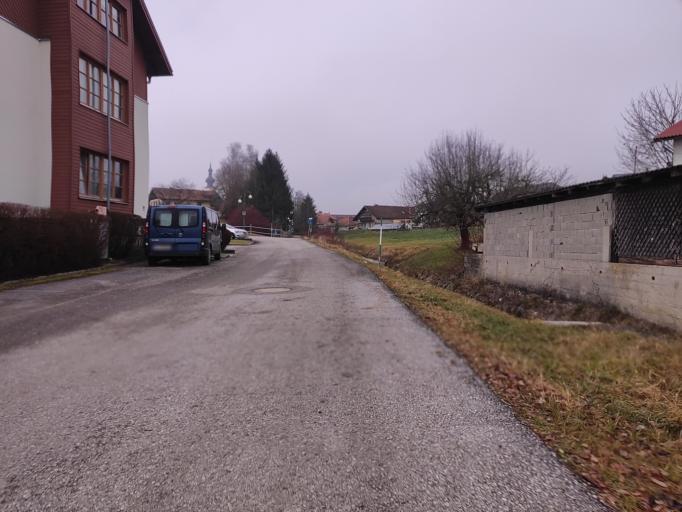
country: AT
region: Salzburg
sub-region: Politischer Bezirk Salzburg-Umgebung
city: Kostendorf
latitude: 47.9570
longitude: 13.2039
